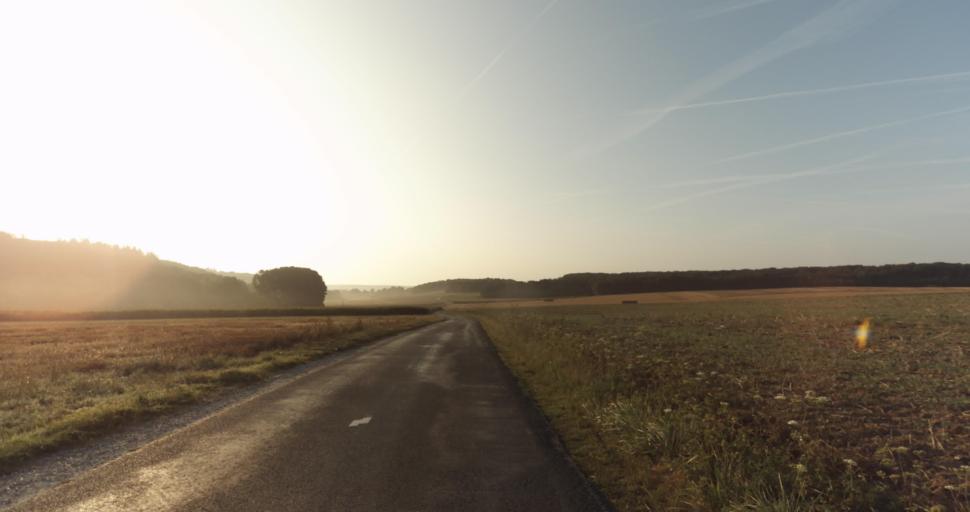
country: FR
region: Haute-Normandie
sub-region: Departement de l'Eure
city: Marcilly-sur-Eure
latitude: 48.7925
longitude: 1.3266
